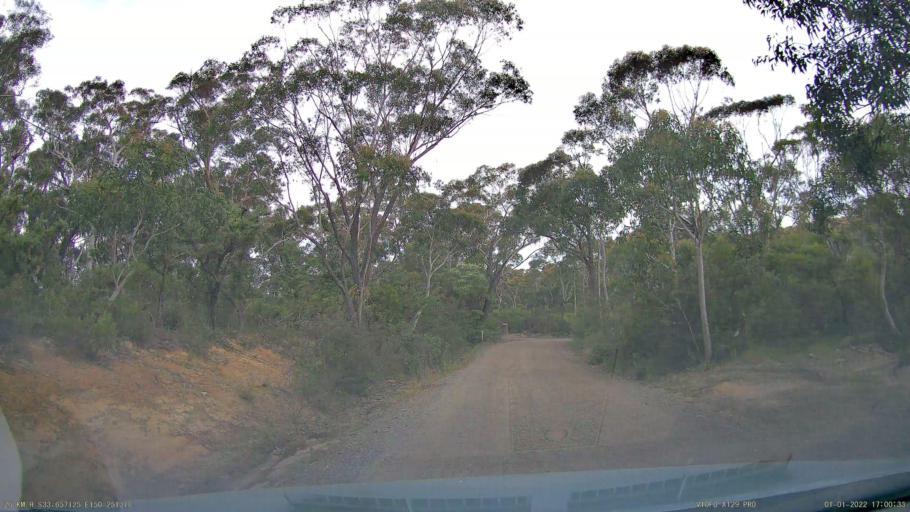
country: AU
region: New South Wales
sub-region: Blue Mountains Municipality
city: Blackheath
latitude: -33.6572
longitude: 150.2514
